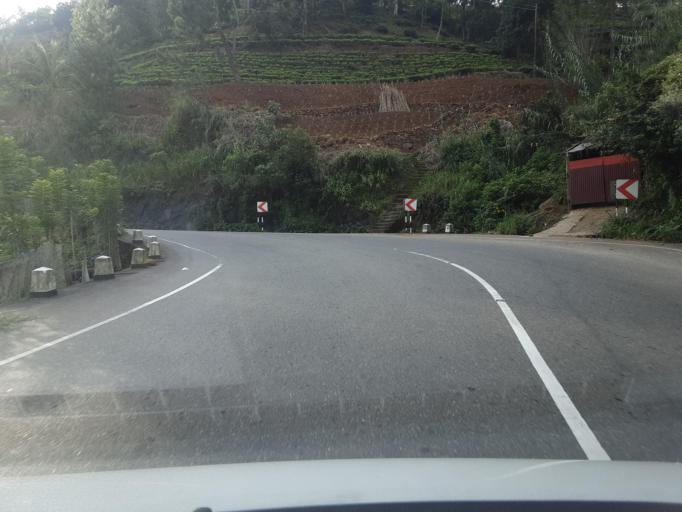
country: LK
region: Uva
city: Badulla
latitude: 6.9308
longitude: 80.9786
